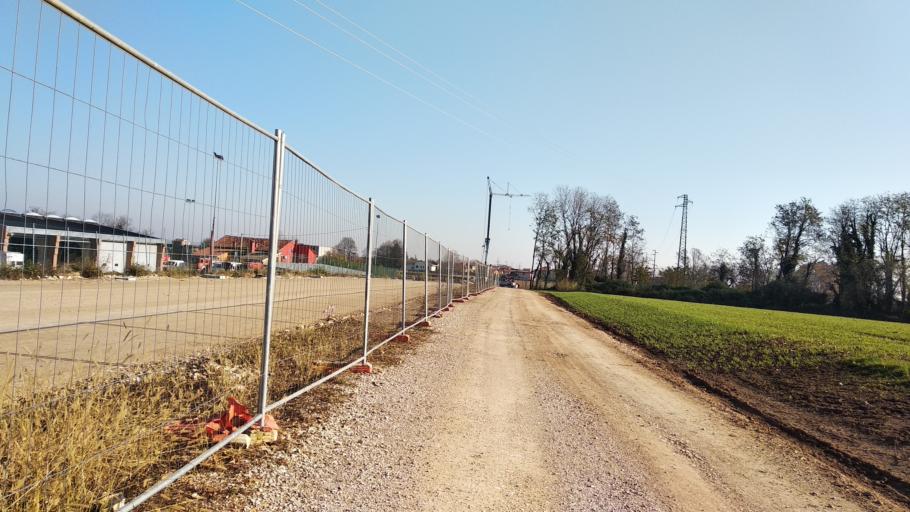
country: IT
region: Veneto
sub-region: Provincia di Vicenza
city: Schio
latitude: 45.7033
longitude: 11.3701
